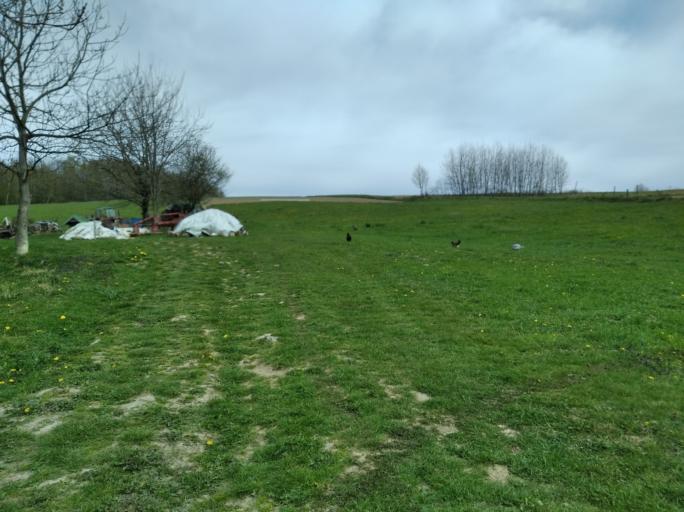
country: PL
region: Subcarpathian Voivodeship
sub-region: Powiat ropczycko-sedziszowski
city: Wielopole Skrzynskie
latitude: 49.9106
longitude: 21.6117
